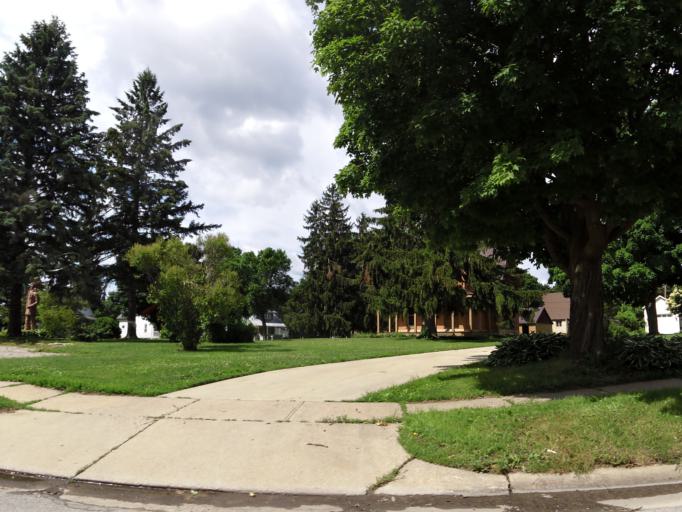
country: US
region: Minnesota
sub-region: Fillmore County
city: Spring Valley
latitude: 43.6917
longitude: -92.3920
